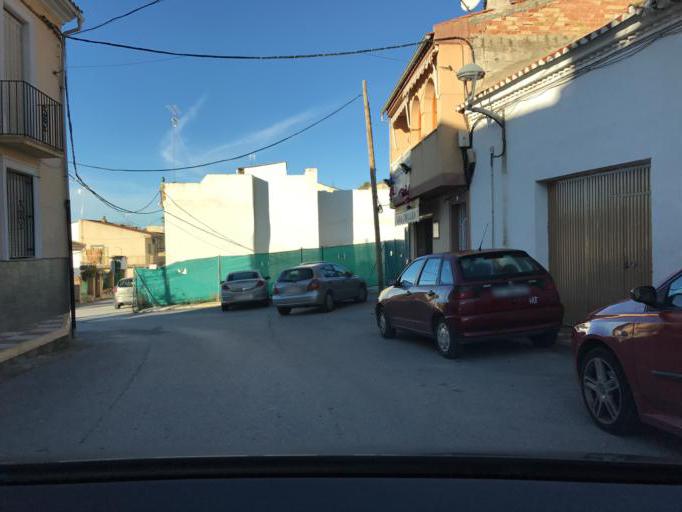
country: ES
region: Andalusia
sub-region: Provincia de Granada
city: Calicasas
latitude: 37.2735
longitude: -3.6188
